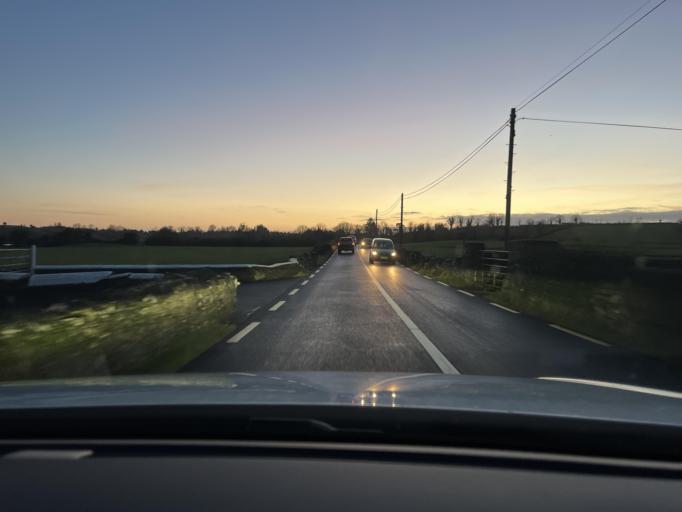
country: IE
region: Connaught
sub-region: County Leitrim
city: Carrick-on-Shannon
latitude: 53.9921
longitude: -8.0362
